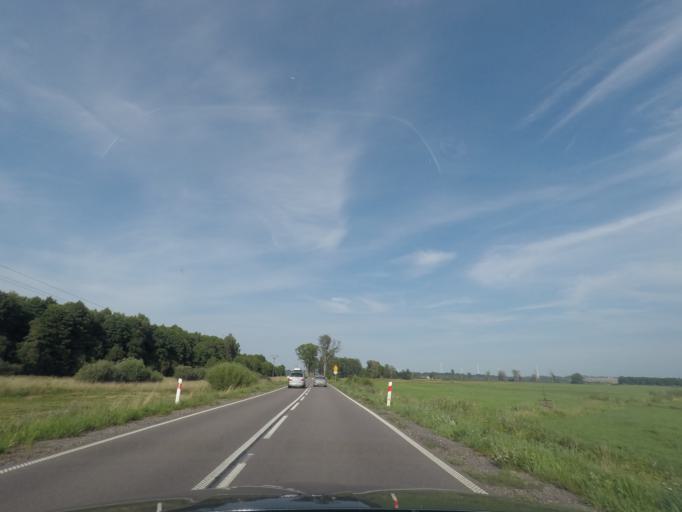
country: PL
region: Pomeranian Voivodeship
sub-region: Powiat leborski
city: Leba
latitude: 54.6554
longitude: 17.5704
